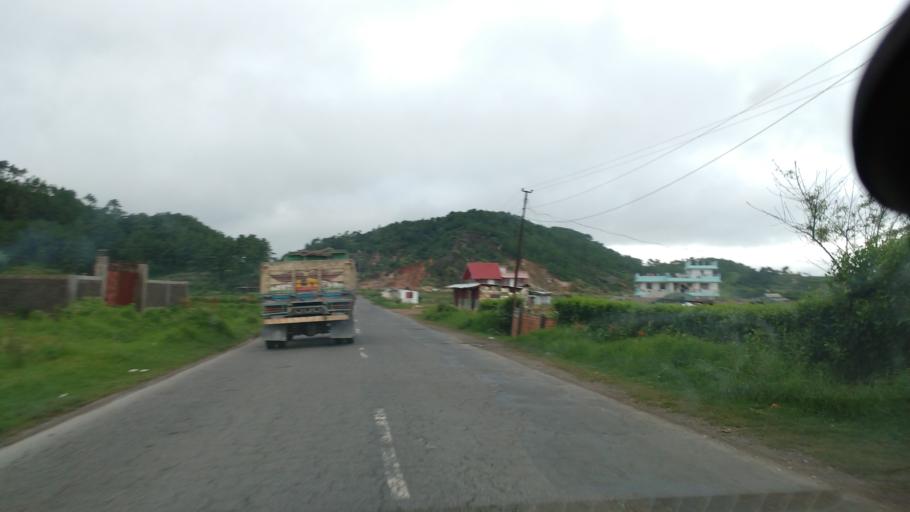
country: IN
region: Meghalaya
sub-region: East Khasi Hills
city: Shillong
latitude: 25.5219
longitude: 91.8160
